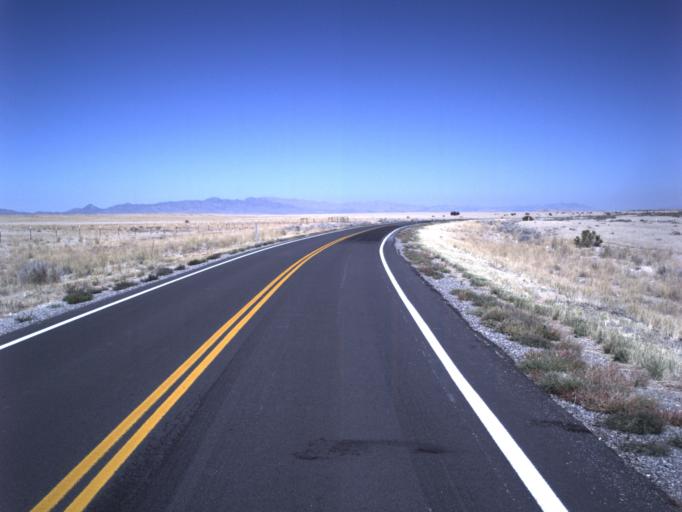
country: US
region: Utah
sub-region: Tooele County
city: Grantsville
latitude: 40.2554
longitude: -112.7395
